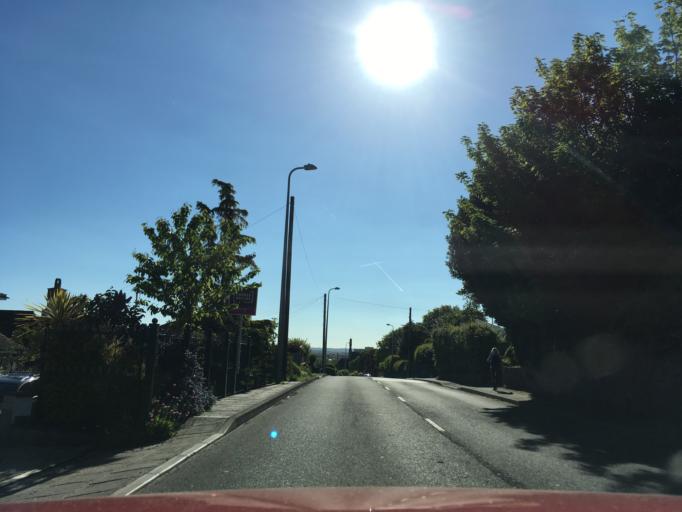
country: GB
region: England
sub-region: North Somerset
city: Portishead
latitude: 51.4872
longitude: -2.7733
